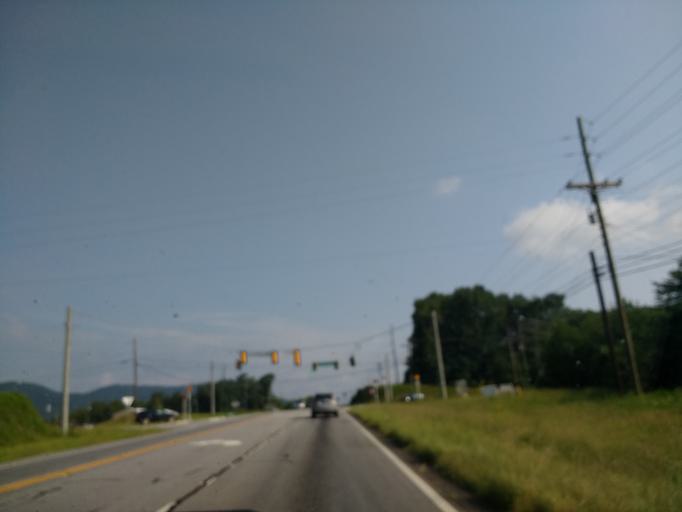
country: US
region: Georgia
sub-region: White County
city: Cleveland
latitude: 34.5417
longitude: -83.7593
